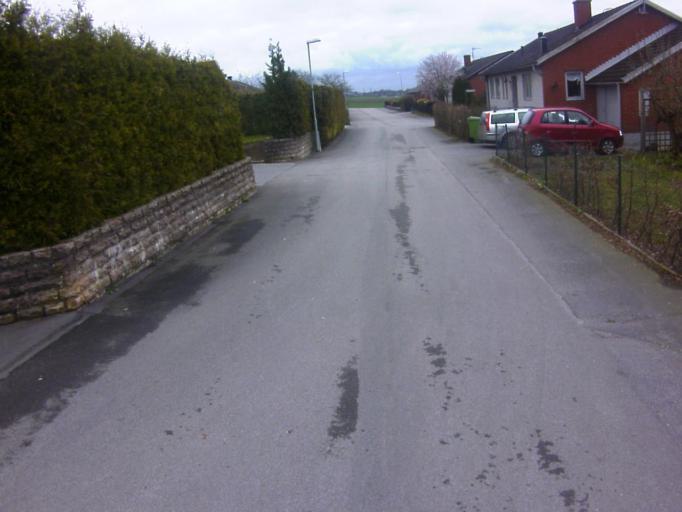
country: SE
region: Skane
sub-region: Lunds Kommun
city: Lund
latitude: 55.7911
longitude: 13.2059
